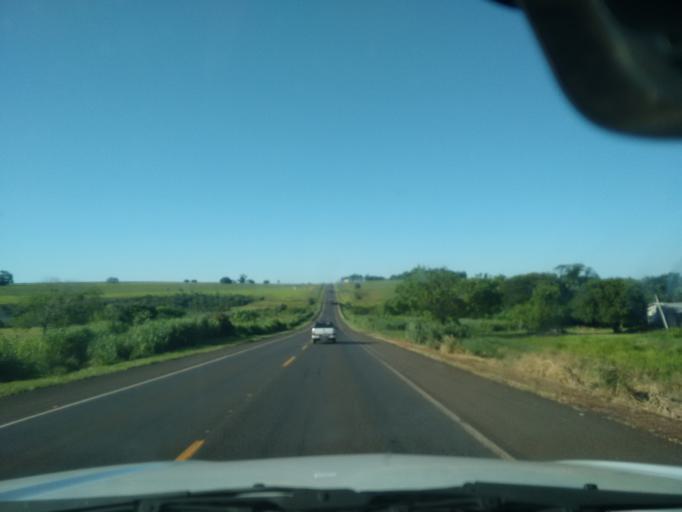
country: PY
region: Canindeyu
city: Salto del Guaira
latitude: -23.9834
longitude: -54.3311
